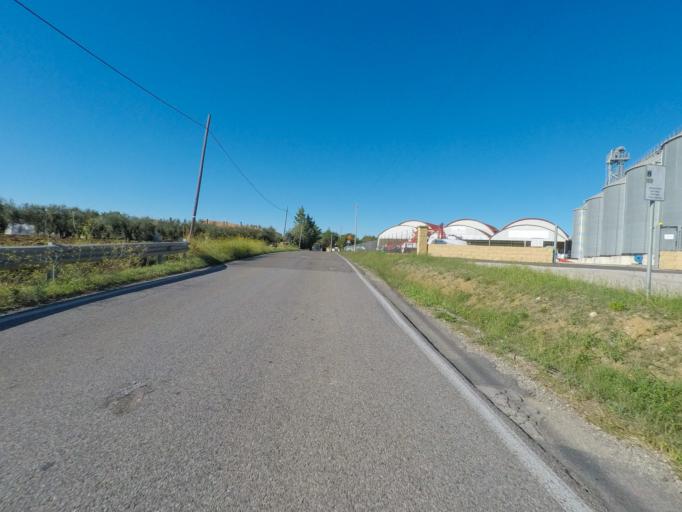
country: IT
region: Tuscany
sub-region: Provincia di Grosseto
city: Grosseto
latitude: 42.7684
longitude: 11.1425
